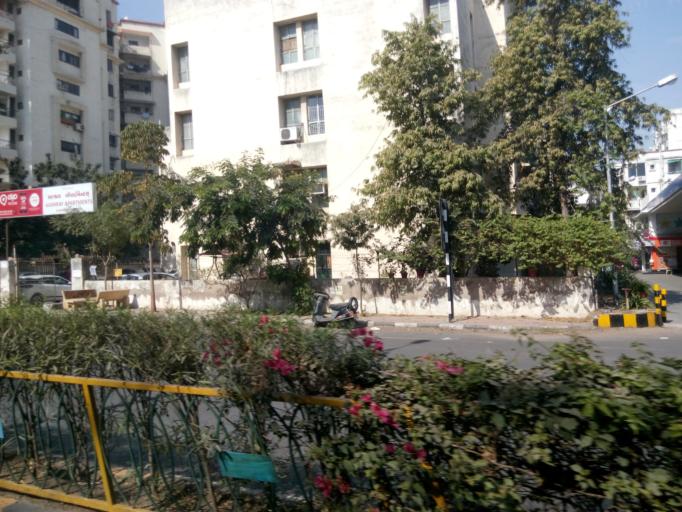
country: IN
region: Gujarat
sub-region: Ahmadabad
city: Sarkhej
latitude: 23.0365
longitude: 72.5146
